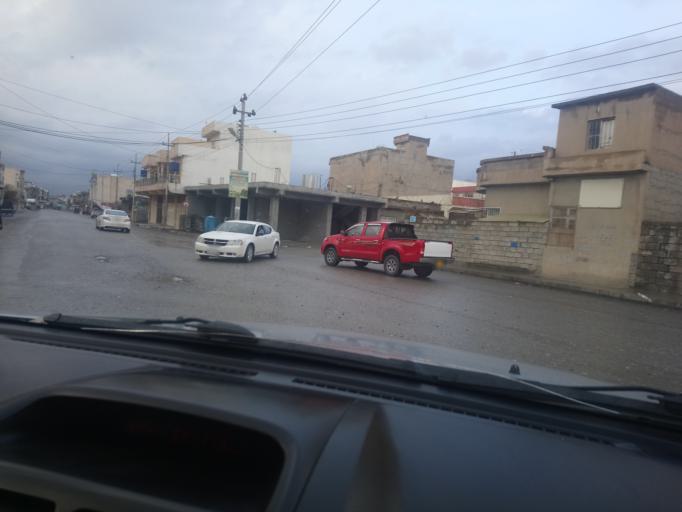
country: IQ
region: As Sulaymaniyah
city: Qeladize
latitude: 36.1831
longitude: 45.1345
